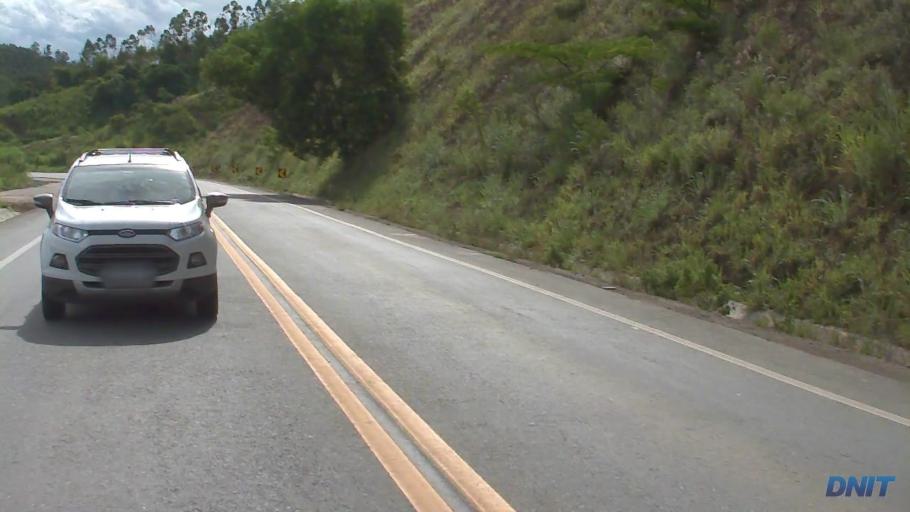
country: BR
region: Minas Gerais
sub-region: Belo Oriente
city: Belo Oriente
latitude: -19.2670
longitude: -42.3536
